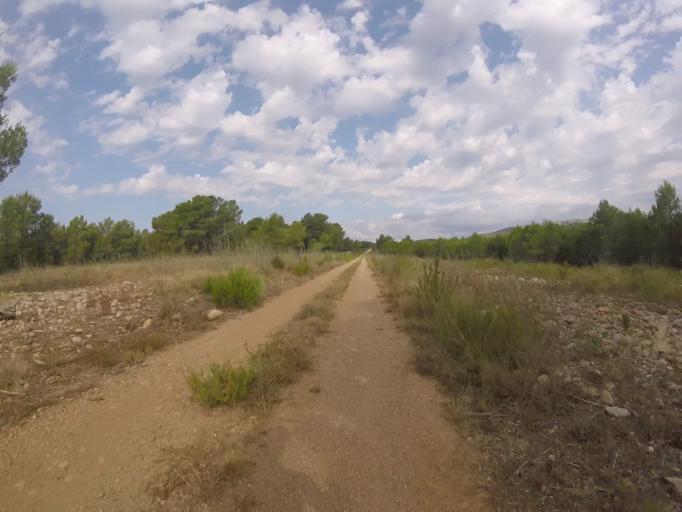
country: ES
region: Valencia
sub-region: Provincia de Castello
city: Alcala de Xivert
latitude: 40.3623
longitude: 0.1994
